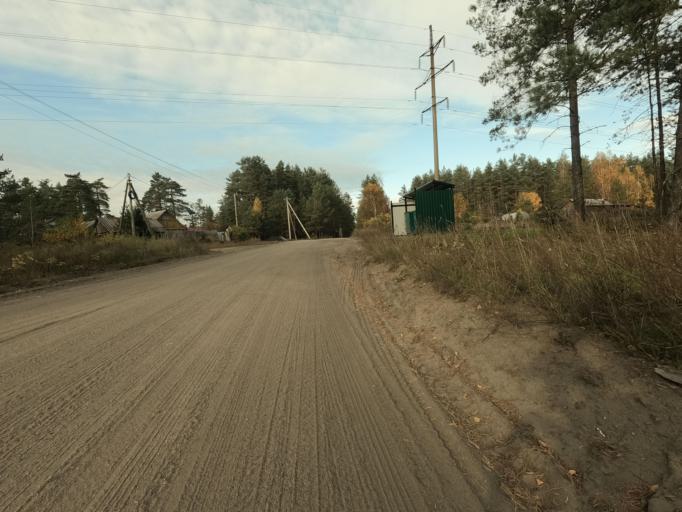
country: RU
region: Leningrad
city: Priladozhskiy
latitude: 59.6326
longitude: 31.3887
